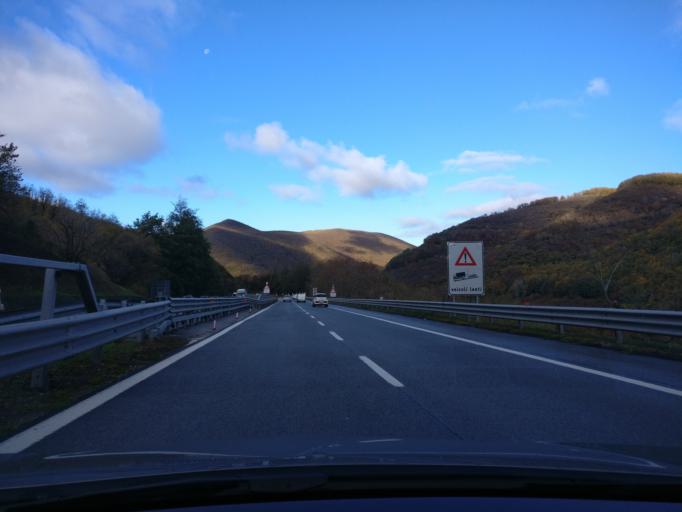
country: IT
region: Campania
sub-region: Provincia di Avellino
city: Moschiano
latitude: 40.9117
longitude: 14.6813
